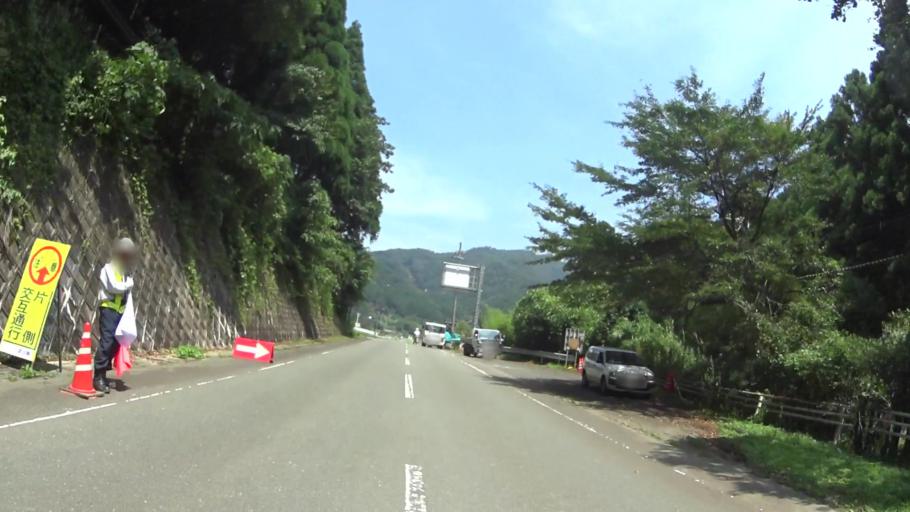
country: JP
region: Kyoto
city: Ayabe
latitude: 35.2965
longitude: 135.4259
